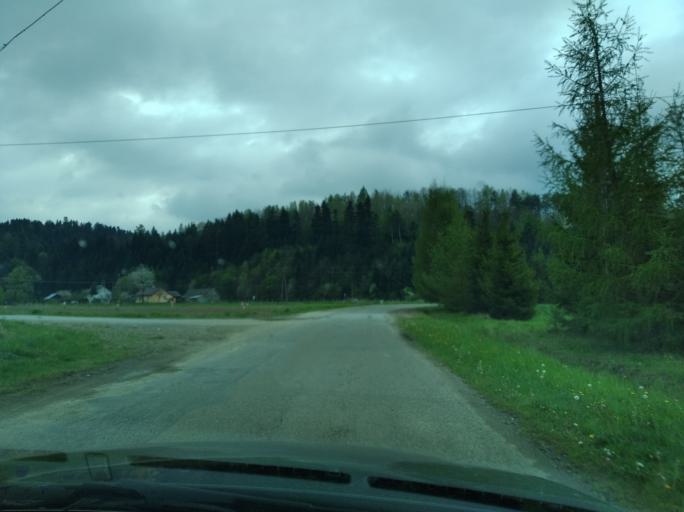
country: PL
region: Subcarpathian Voivodeship
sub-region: Powiat brzozowski
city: Dydnia
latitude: 49.6980
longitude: 22.1973
